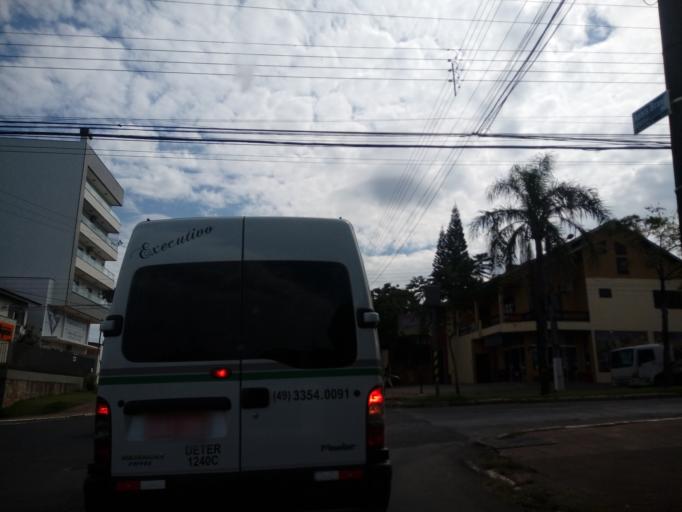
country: BR
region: Santa Catarina
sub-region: Chapeco
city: Chapeco
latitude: -27.1059
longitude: -52.6043
